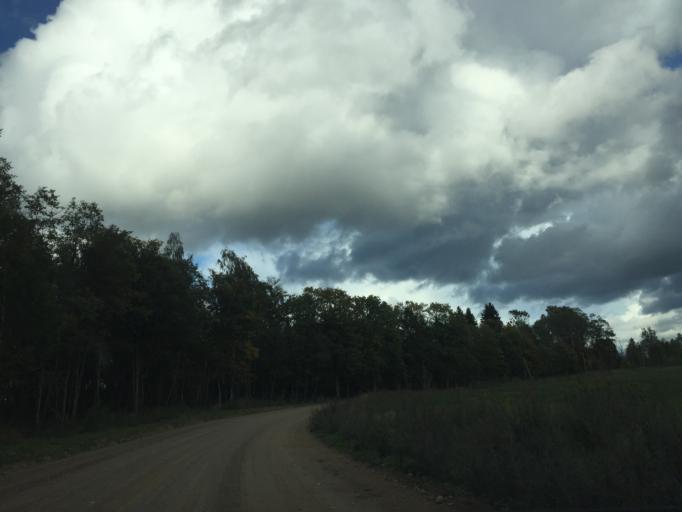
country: LV
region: Malpils
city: Malpils
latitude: 57.0592
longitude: 25.1425
